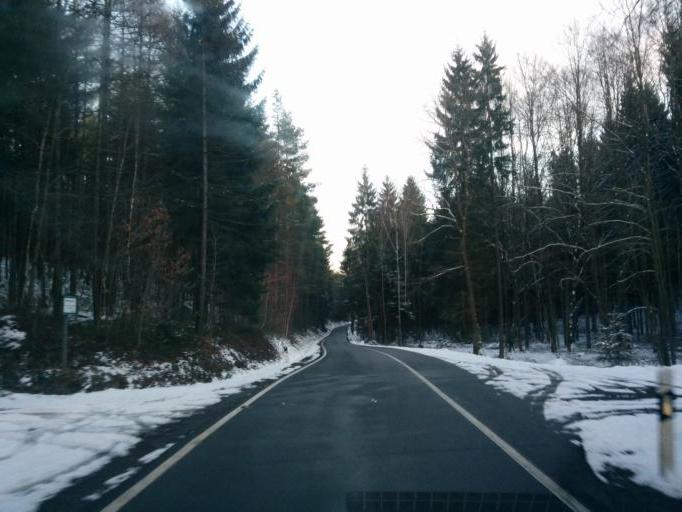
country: DE
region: Saxony
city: Floha
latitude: 50.8431
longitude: 13.0566
